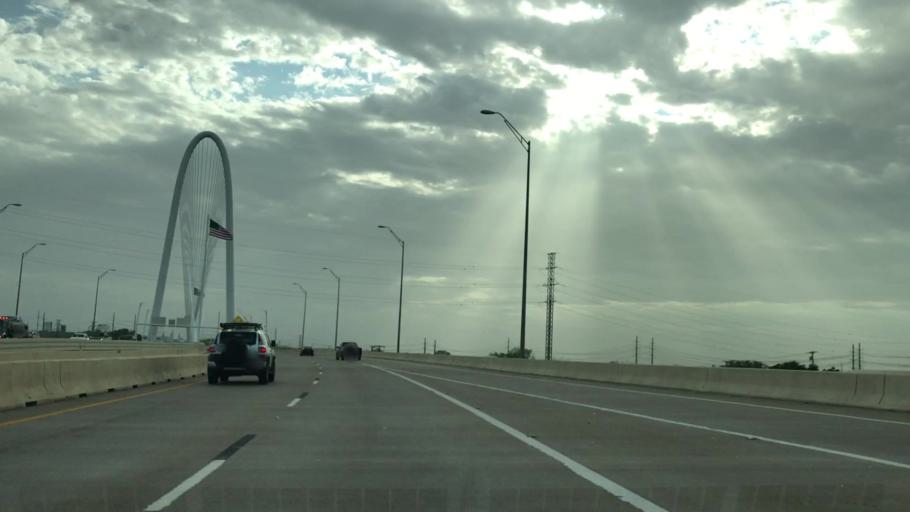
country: US
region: Texas
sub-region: Dallas County
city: Dallas
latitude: 32.7817
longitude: -96.8170
